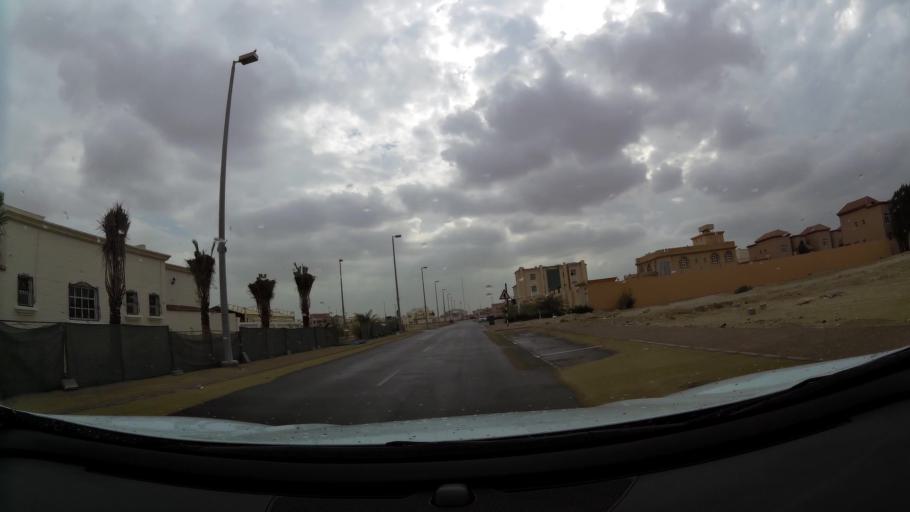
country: AE
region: Abu Dhabi
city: Abu Dhabi
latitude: 24.3579
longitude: 54.6159
